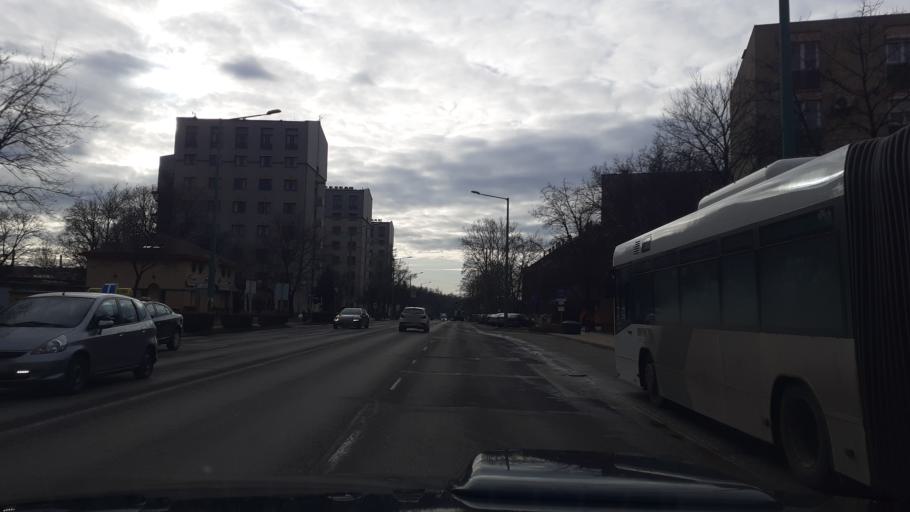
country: HU
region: Fejer
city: dunaujvaros
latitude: 46.9619
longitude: 18.9327
